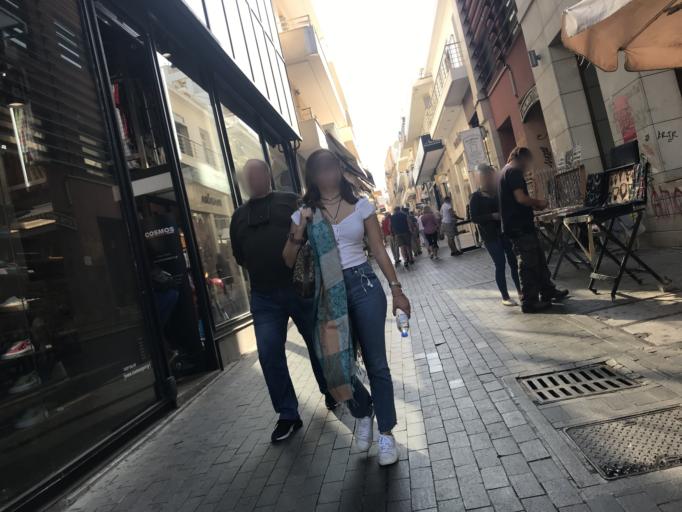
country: GR
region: Crete
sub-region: Nomos Irakleiou
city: Irakleion
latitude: 35.3391
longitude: 25.1333
